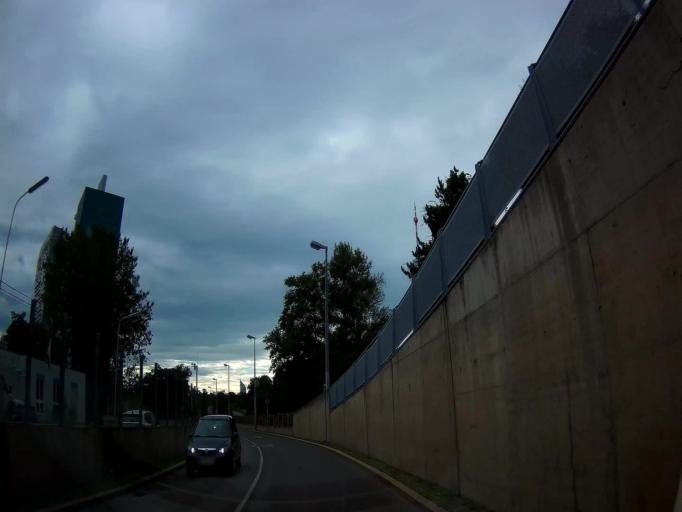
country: AT
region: Vienna
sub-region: Wien Stadt
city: Vienna
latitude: 48.2369
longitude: 16.4170
